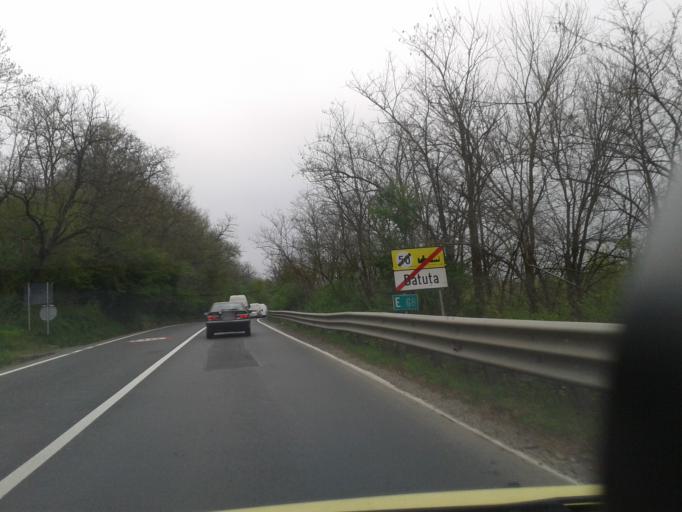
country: RO
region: Arad
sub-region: Comuna Bata
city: Bata
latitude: 46.0372
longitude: 22.0615
